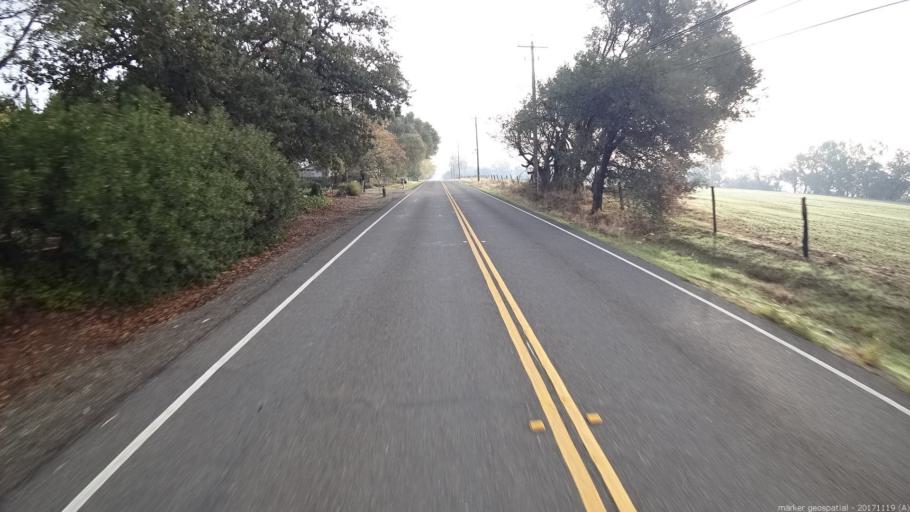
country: US
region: California
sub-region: Shasta County
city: Anderson
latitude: 40.4804
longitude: -122.2873
